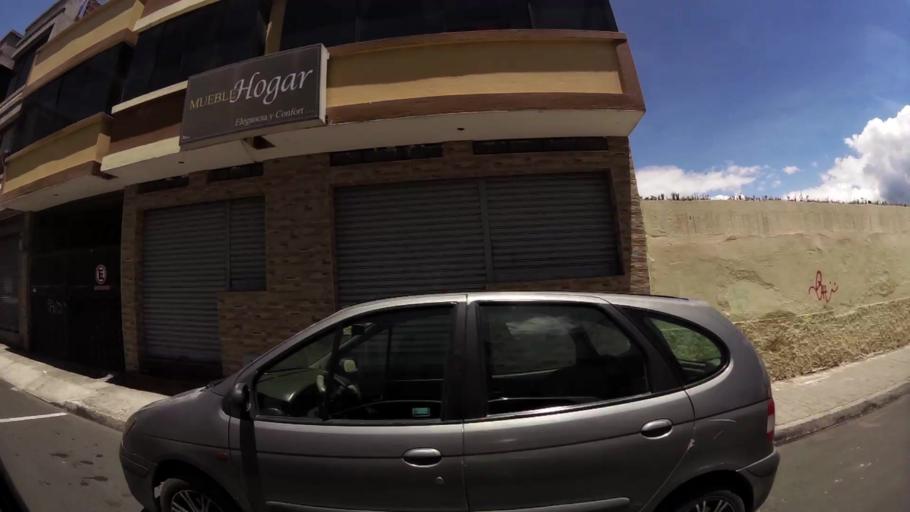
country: EC
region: Chimborazo
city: Riobamba
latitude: -1.6721
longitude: -78.6428
